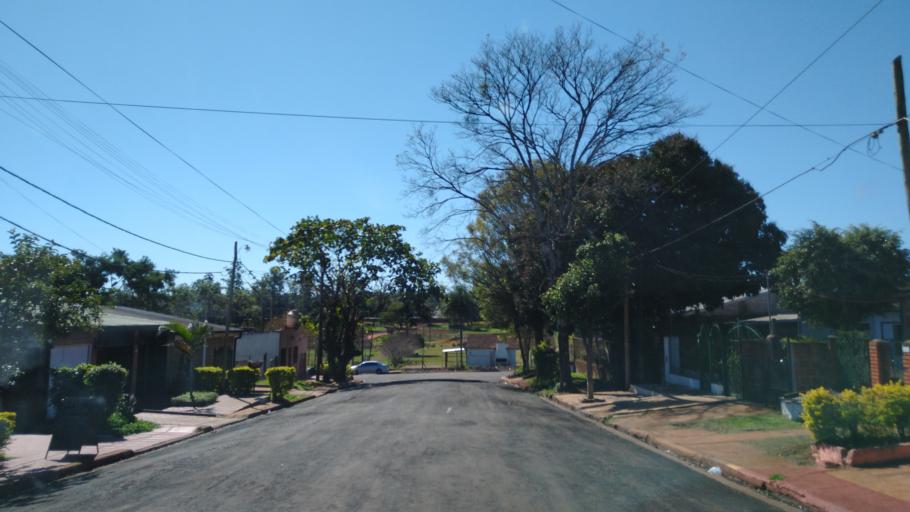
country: AR
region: Misiones
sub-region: Departamento de Capital
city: Posadas
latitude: -27.3948
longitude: -55.9336
